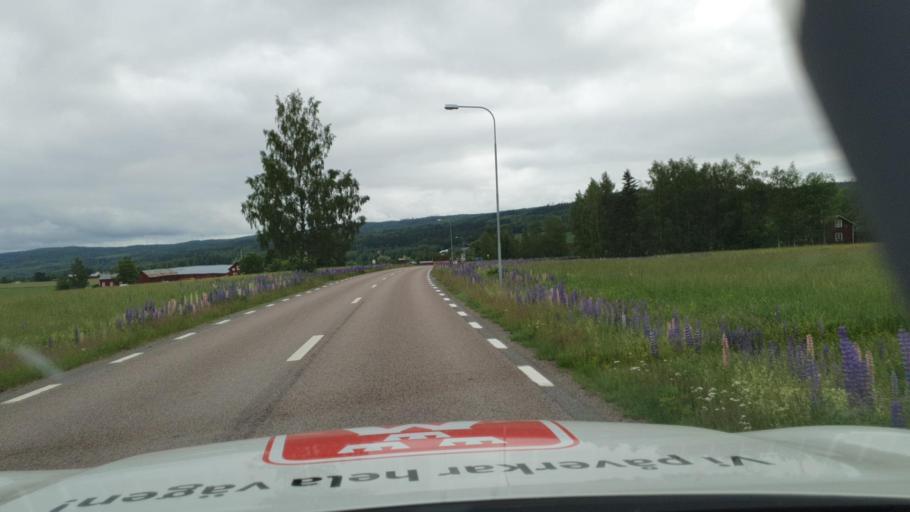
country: SE
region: Vaermland
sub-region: Sunne Kommun
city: Sunne
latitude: 59.8592
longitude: 12.9457
